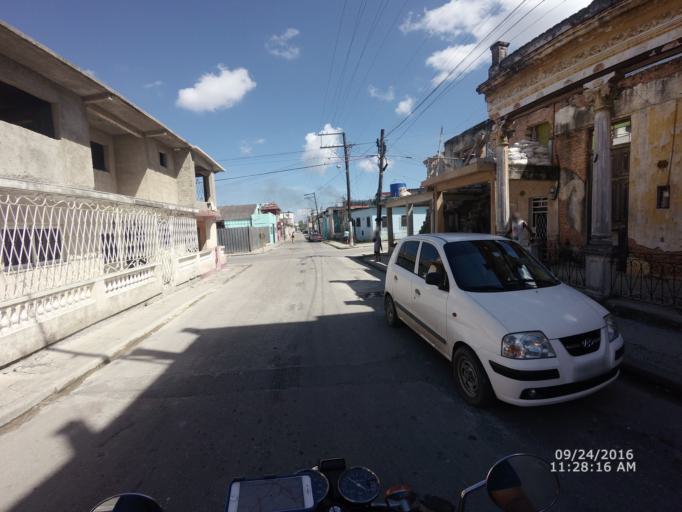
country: CU
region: La Habana
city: Cerro
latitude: 23.1114
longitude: -82.3647
